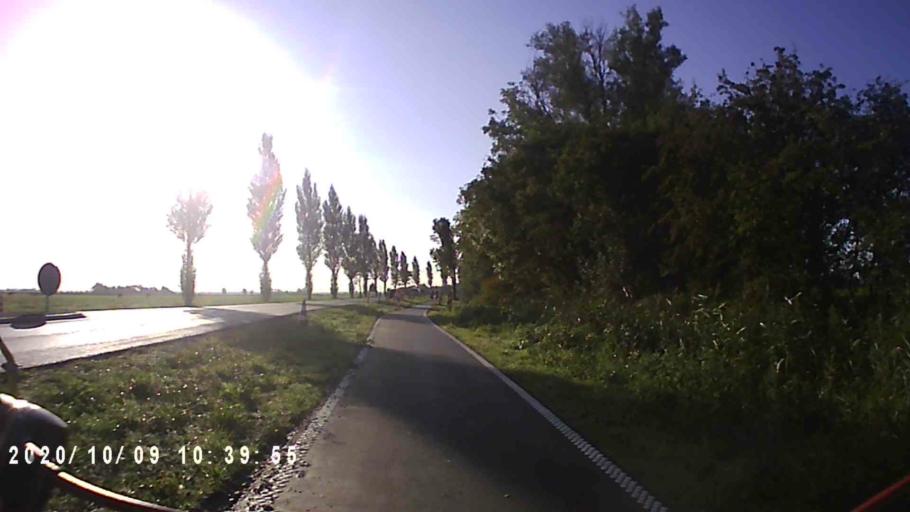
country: NL
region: Groningen
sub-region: Gemeente Winsum
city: Winsum
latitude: 53.2832
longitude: 6.5348
